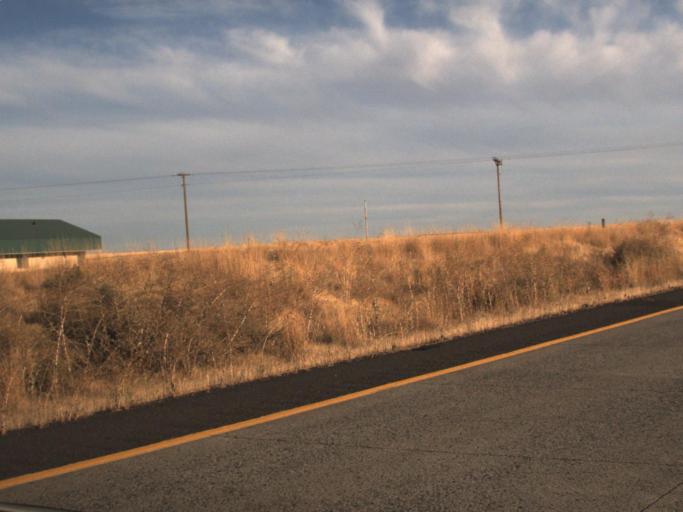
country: US
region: Washington
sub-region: Franklin County
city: Connell
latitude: 46.7202
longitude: -118.8344
